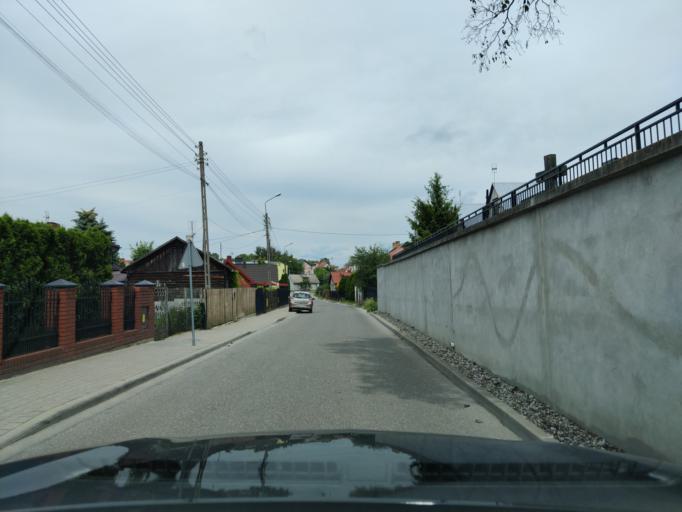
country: PL
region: Masovian Voivodeship
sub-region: Powiat wyszkowski
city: Wyszkow
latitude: 52.5984
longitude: 21.4587
